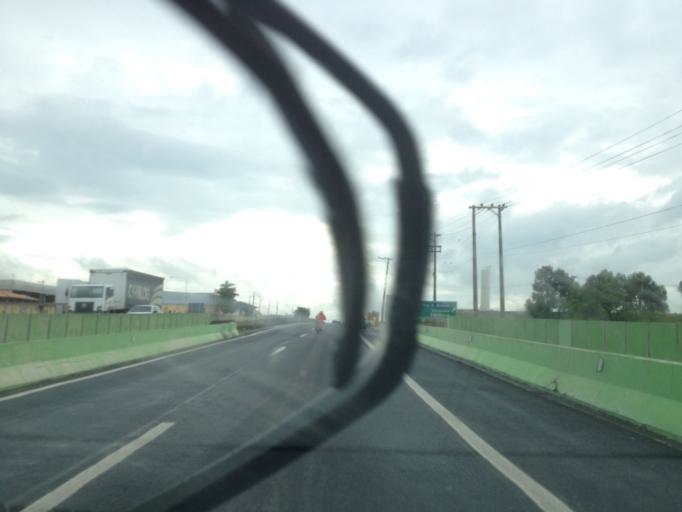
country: BR
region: Sao Paulo
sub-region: Itu
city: Itu
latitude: -23.2540
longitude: -47.3204
